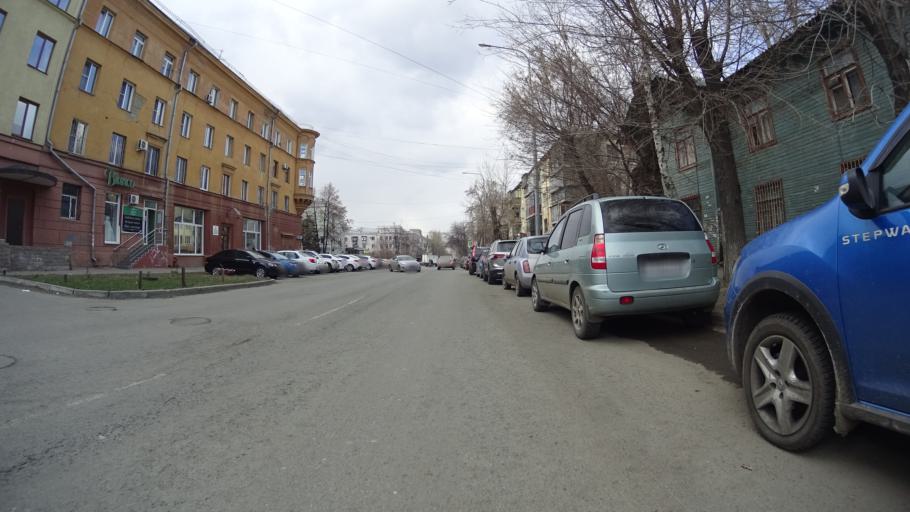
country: RU
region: Chelyabinsk
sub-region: Gorod Chelyabinsk
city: Chelyabinsk
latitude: 55.1572
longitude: 61.4101
